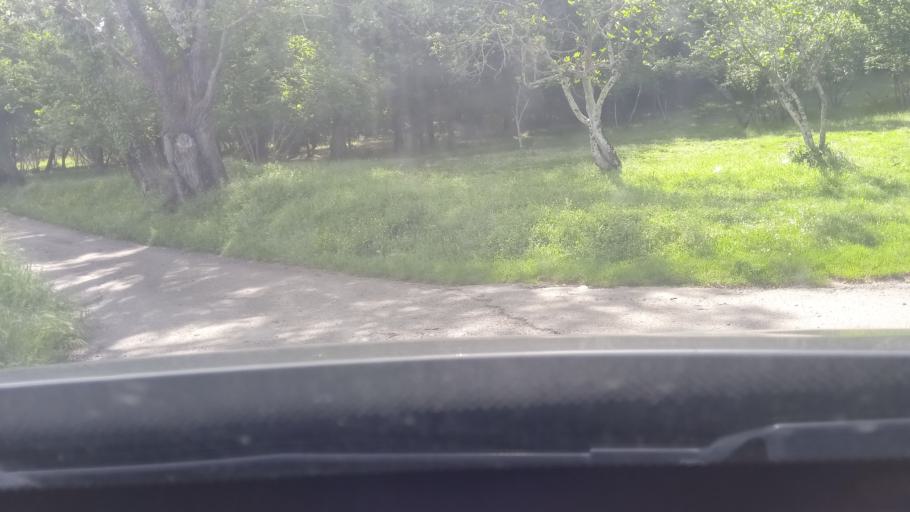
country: IT
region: Latium
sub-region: Provincia di Latina
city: Grunuovo-Campomaggiore San Luca
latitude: 41.2797
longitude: 13.7667
